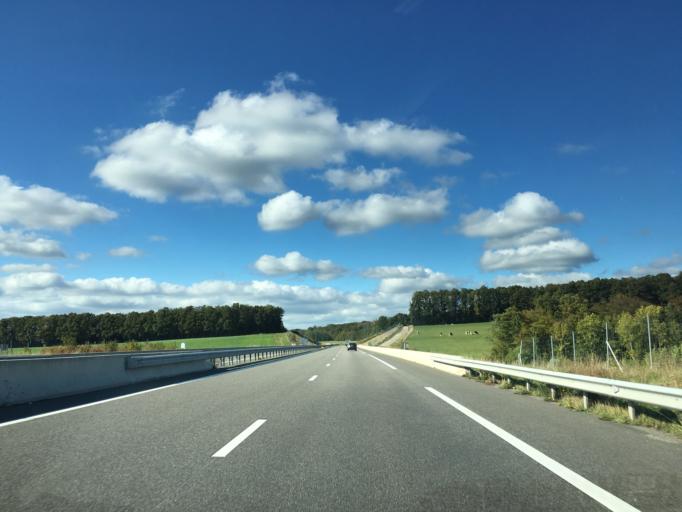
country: FR
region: Lorraine
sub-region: Departement de Meurthe-et-Moselle
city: Baccarat
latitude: 48.4947
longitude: 6.7012
